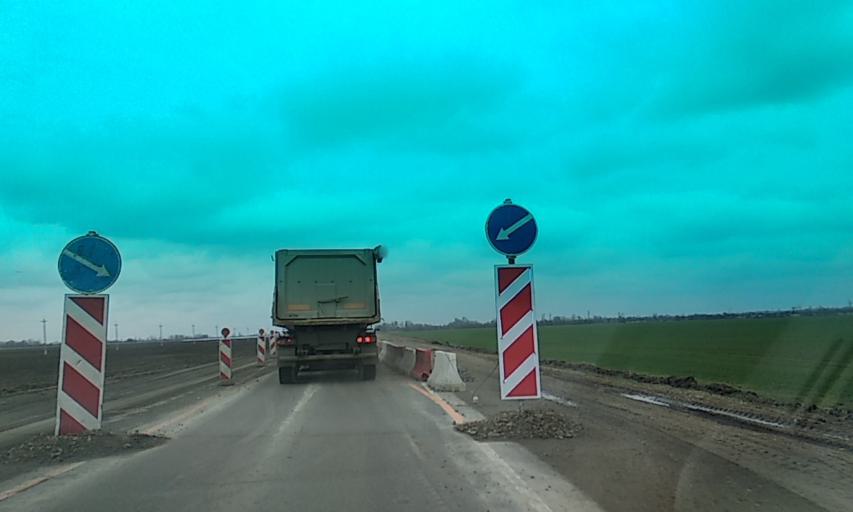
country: RU
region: Adygeya
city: Beloye
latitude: 45.0235
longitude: 39.6874
